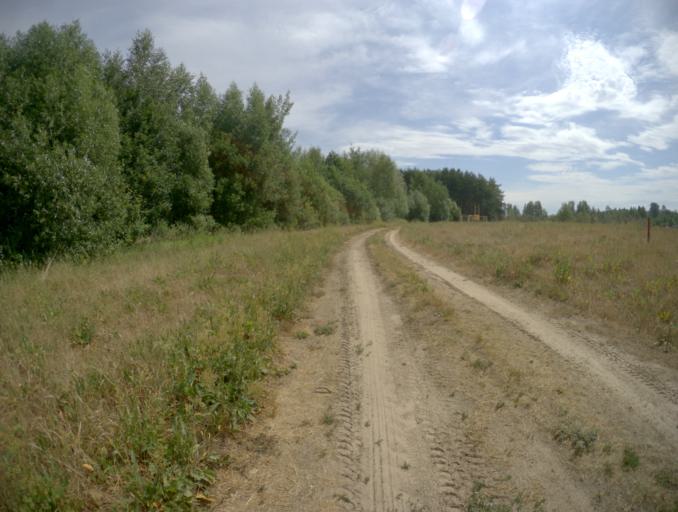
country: RU
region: Vladimir
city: Raduzhnyy
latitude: 56.0292
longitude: 40.3187
